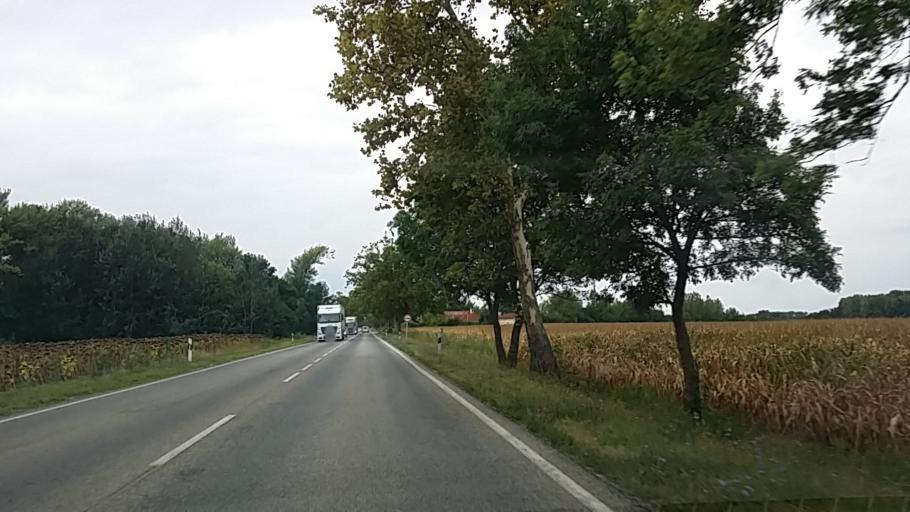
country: HU
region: Gyor-Moson-Sopron
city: Kapuvar
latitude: 47.5880
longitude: 17.0922
